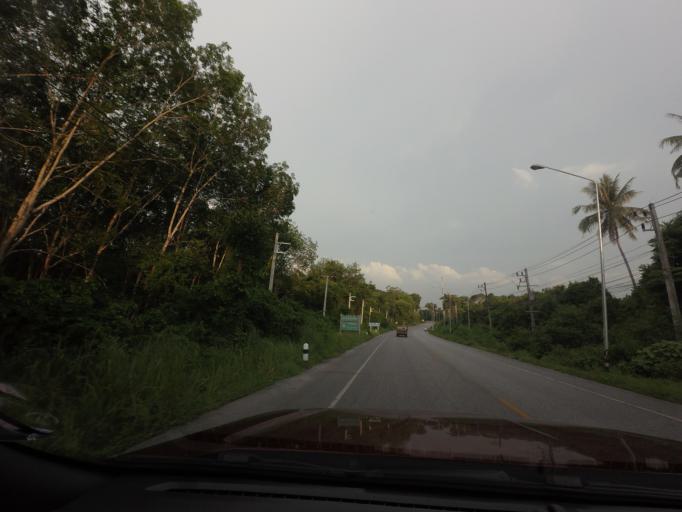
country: TH
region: Pattani
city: Mae Lan
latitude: 6.6705
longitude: 101.1587
